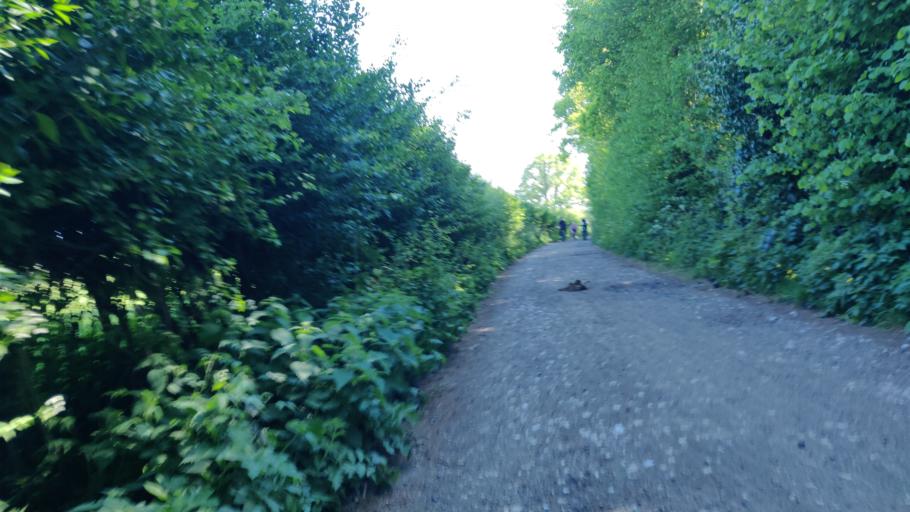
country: GB
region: England
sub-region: West Sussex
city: Southwater
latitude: 51.0583
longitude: -0.3732
